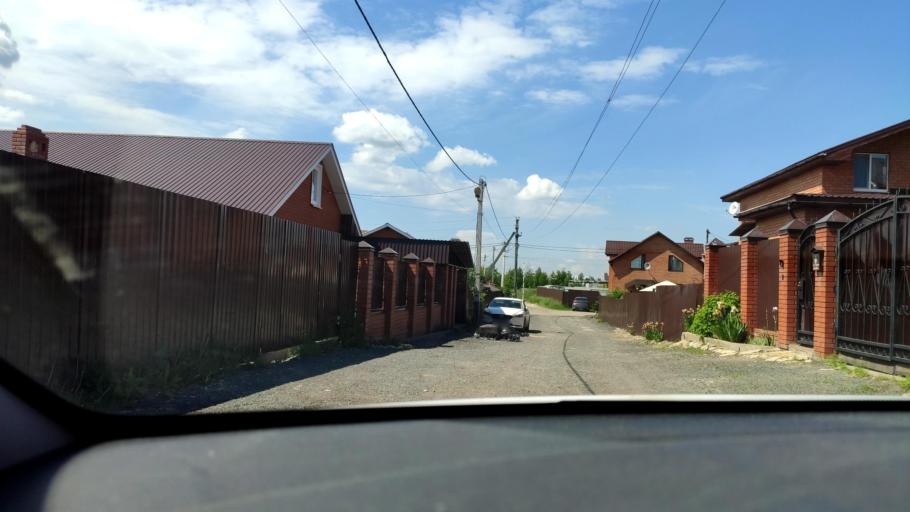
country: RU
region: Tatarstan
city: Stolbishchi
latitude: 55.7534
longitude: 49.2736
